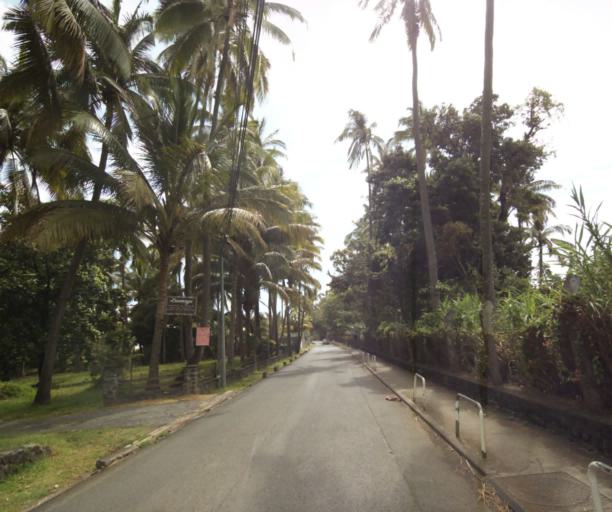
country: RE
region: Reunion
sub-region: Reunion
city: Saint-Paul
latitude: -21.0110
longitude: 55.2826
